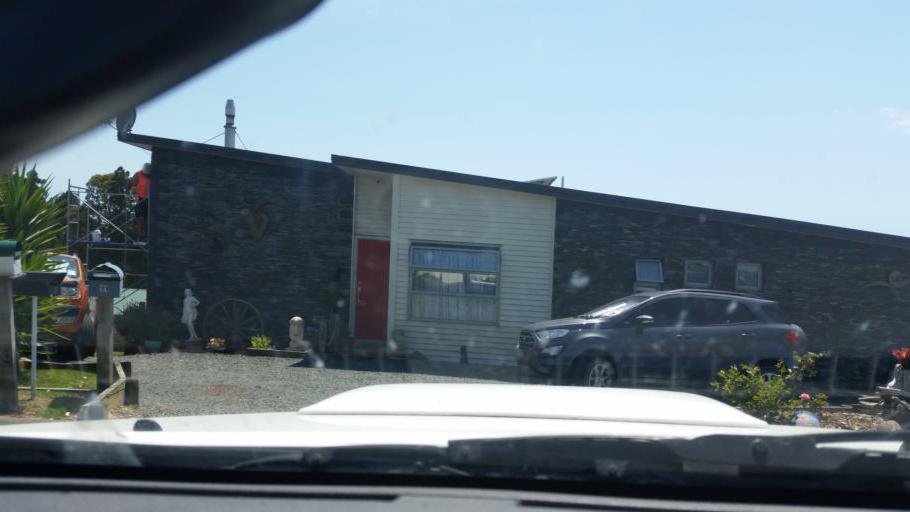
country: NZ
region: Auckland
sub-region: Auckland
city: Wellsford
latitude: -36.1236
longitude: 174.5721
